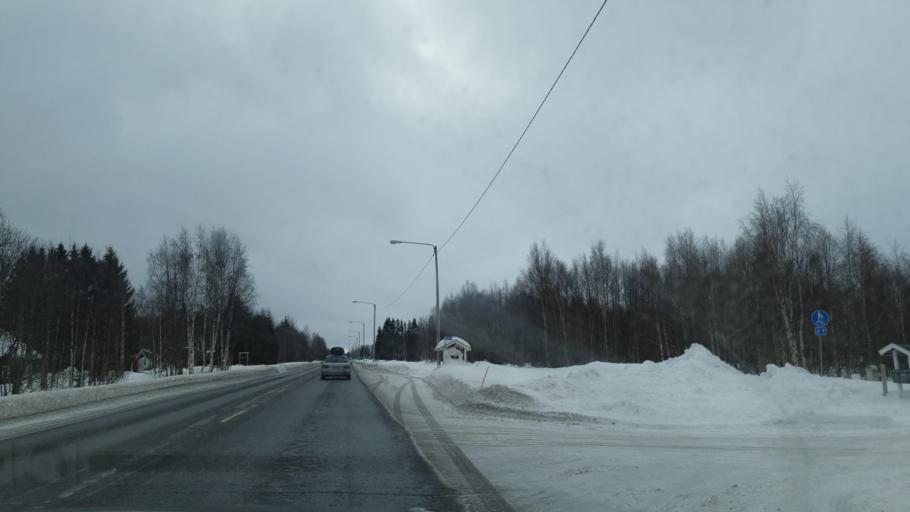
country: FI
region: Lapland
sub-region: Kemi-Tornio
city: Tornio
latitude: 65.8866
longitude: 24.1518
